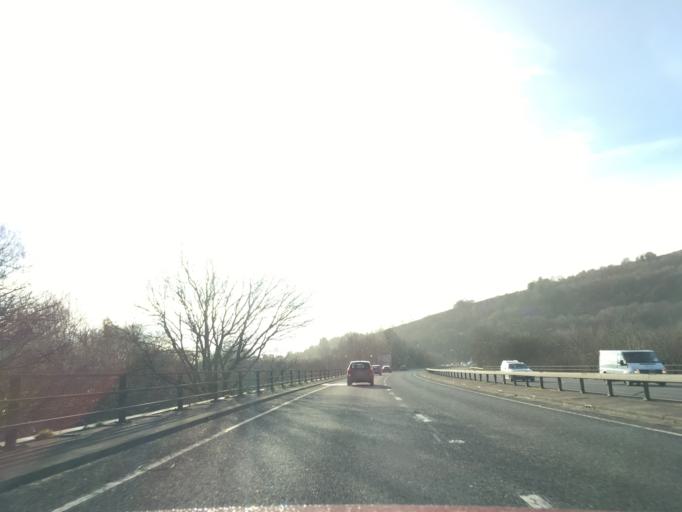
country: GB
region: Wales
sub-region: Caerphilly County Borough
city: Llanbradach
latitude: 51.6001
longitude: -3.2276
